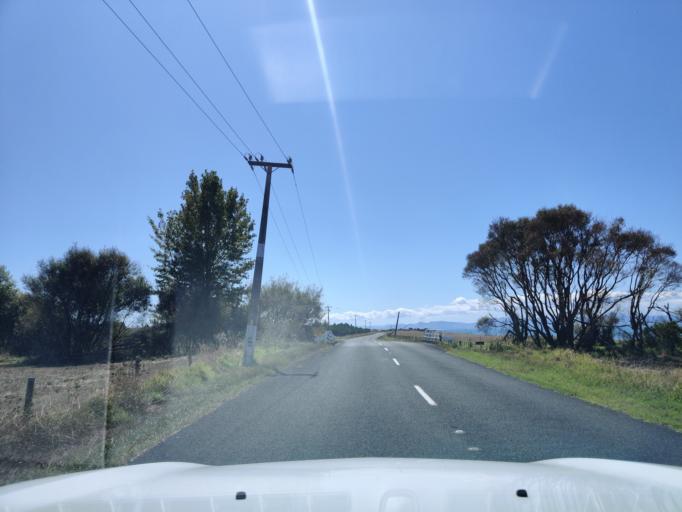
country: NZ
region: Waikato
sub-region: Thames-Coromandel District
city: Thames
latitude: -37.0679
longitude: 175.2962
